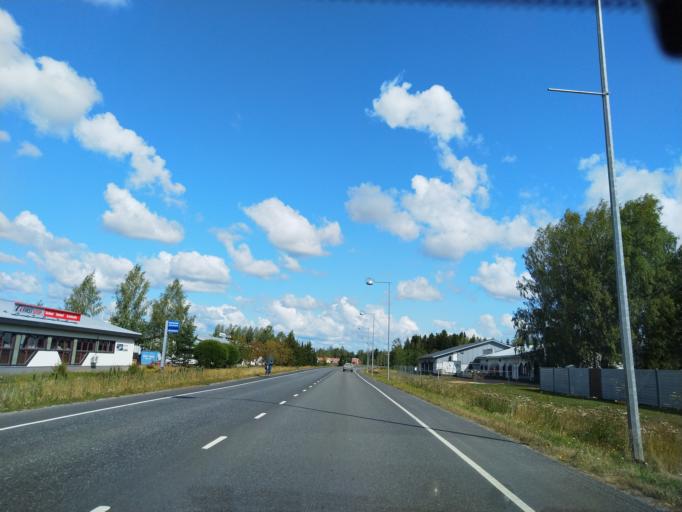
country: FI
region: Satakunta
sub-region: Pori
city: Huittinen
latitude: 61.1693
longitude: 22.7081
